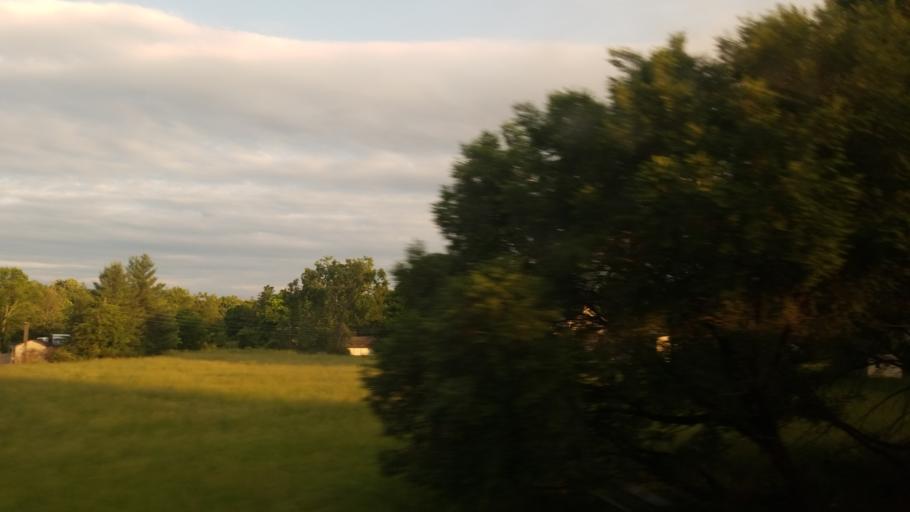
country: US
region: Virginia
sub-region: Prince William County
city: Nokesville
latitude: 38.6541
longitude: -77.6393
